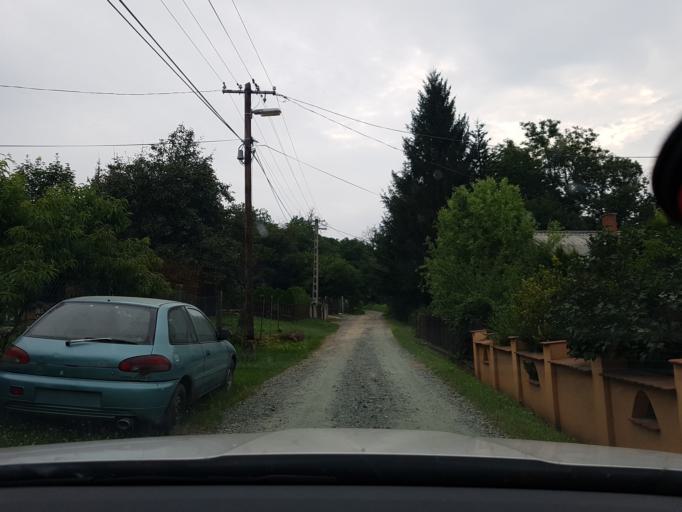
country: HU
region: Vas
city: Koszeg
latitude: 47.3474
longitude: 16.4971
